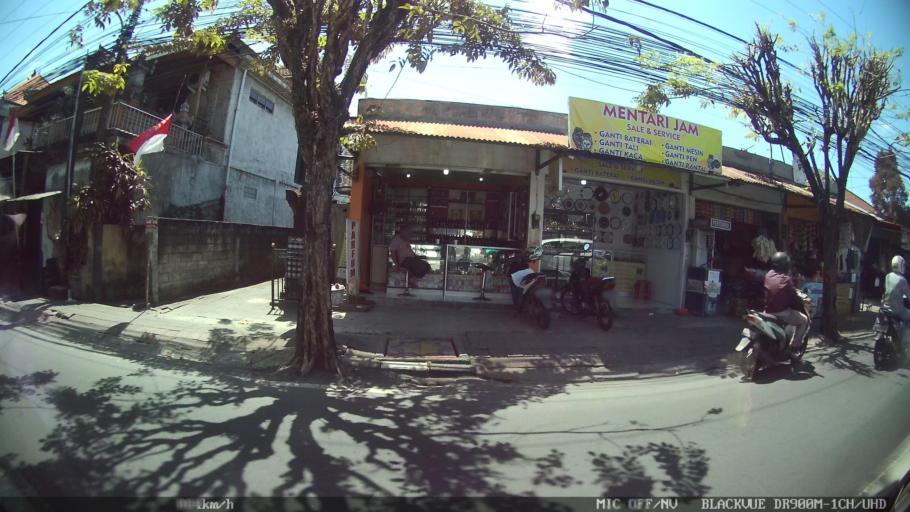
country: ID
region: Bali
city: Banjar Gunungpande
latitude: -8.6454
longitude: 115.1598
